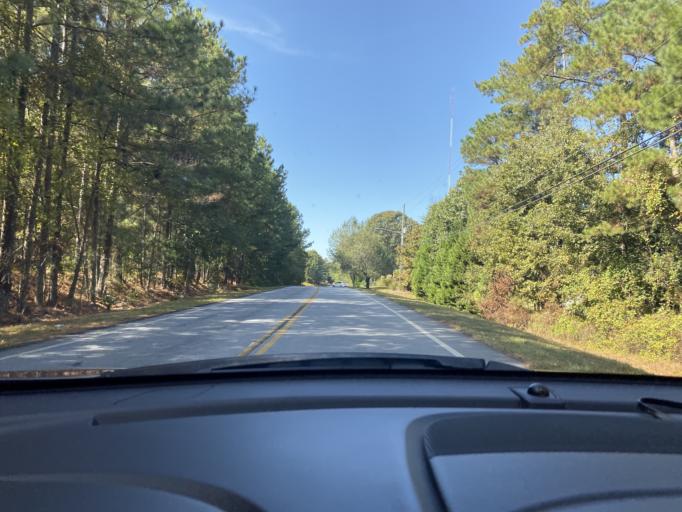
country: US
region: Georgia
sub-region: Gwinnett County
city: Grayson
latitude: 33.8974
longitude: -83.9094
